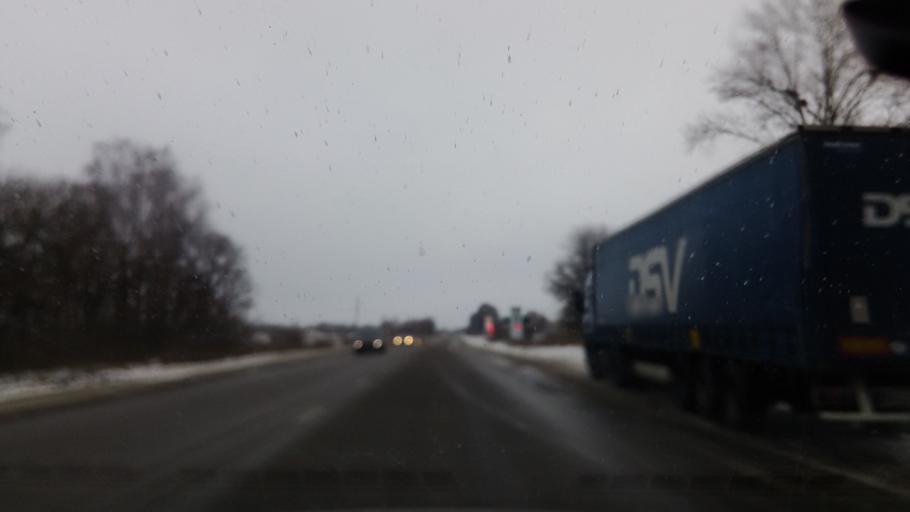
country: RU
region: Tula
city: Bolokhovo
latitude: 54.0633
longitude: 37.8010
